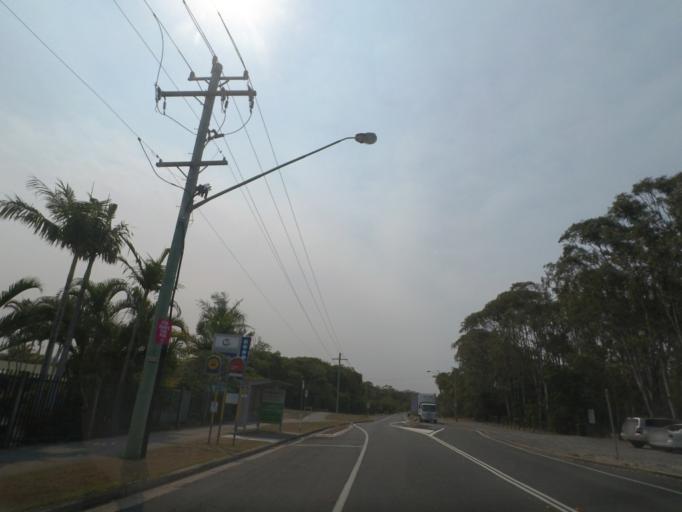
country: AU
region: New South Wales
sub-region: Tweed
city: Pottsville Beach
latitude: -28.3549
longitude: 153.5727
